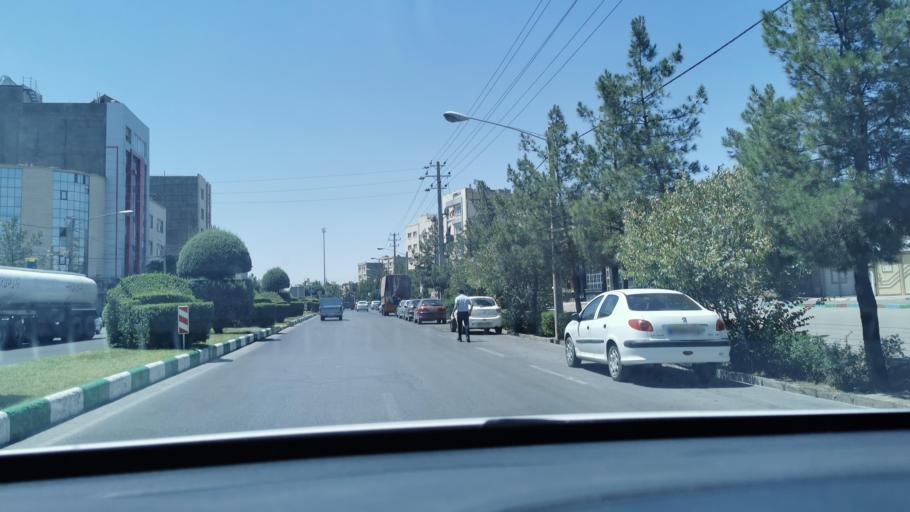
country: IR
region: Razavi Khorasan
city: Mashhad
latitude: 36.3392
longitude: 59.4852
